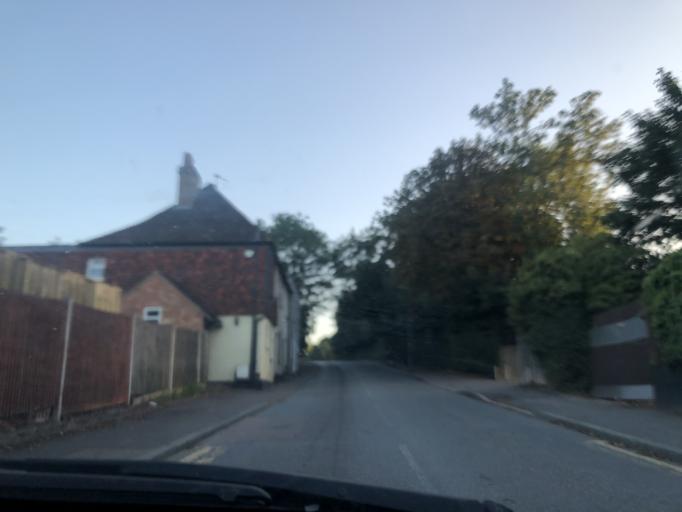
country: GB
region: England
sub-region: Kent
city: Dartford
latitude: 51.4332
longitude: 0.2158
